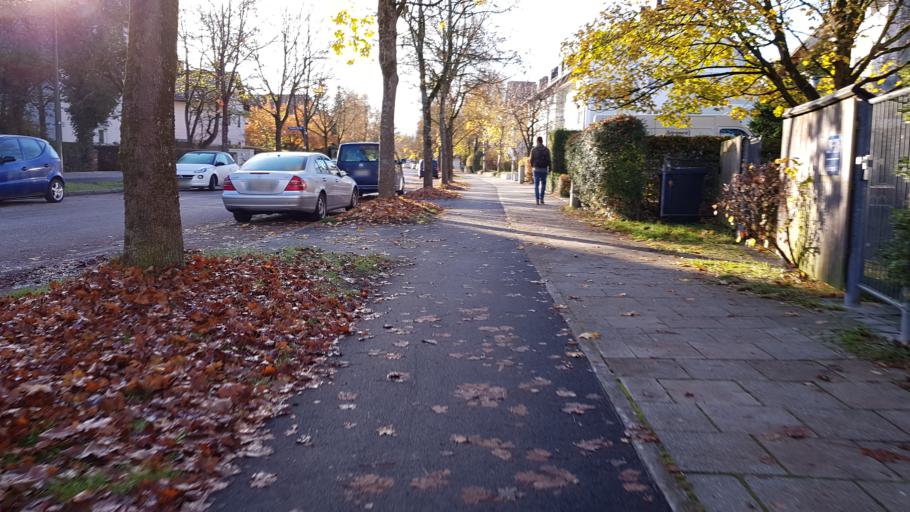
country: DE
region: Bavaria
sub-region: Upper Bavaria
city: Neubiberg
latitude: 48.0975
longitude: 11.6315
